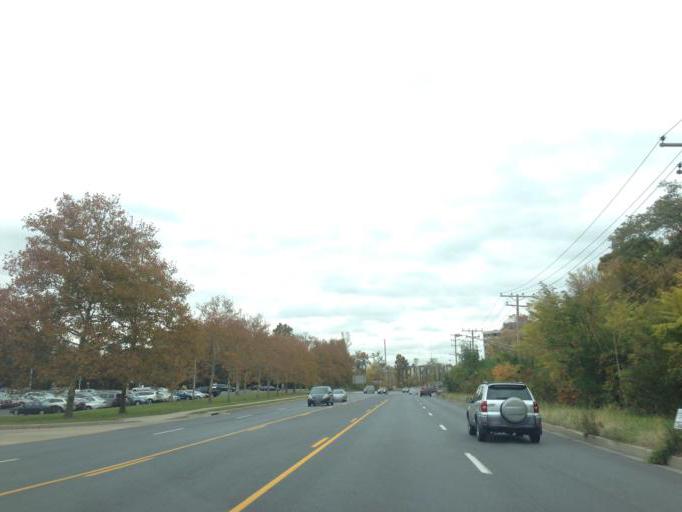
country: US
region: Maryland
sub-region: Baltimore County
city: Owings Mills
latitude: 39.4085
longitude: -76.7788
